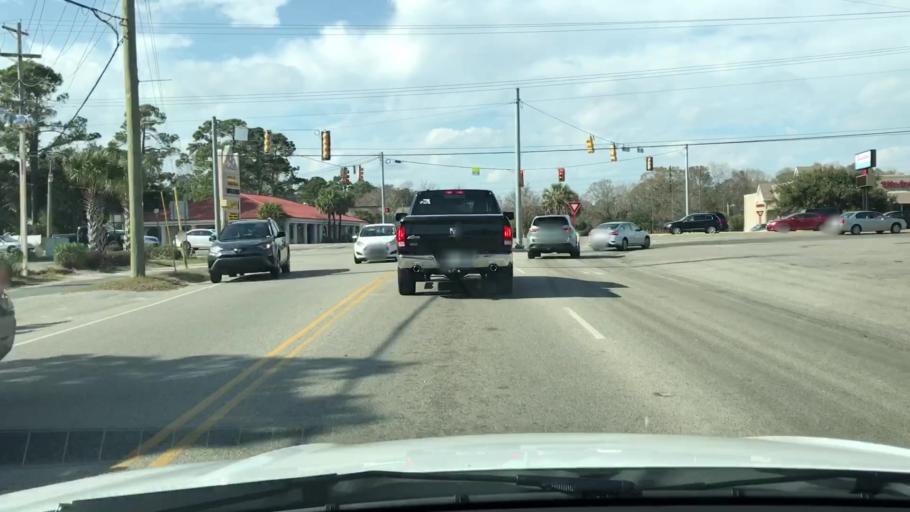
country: US
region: South Carolina
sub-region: Horry County
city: Garden City
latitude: 33.5856
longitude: -79.0118
